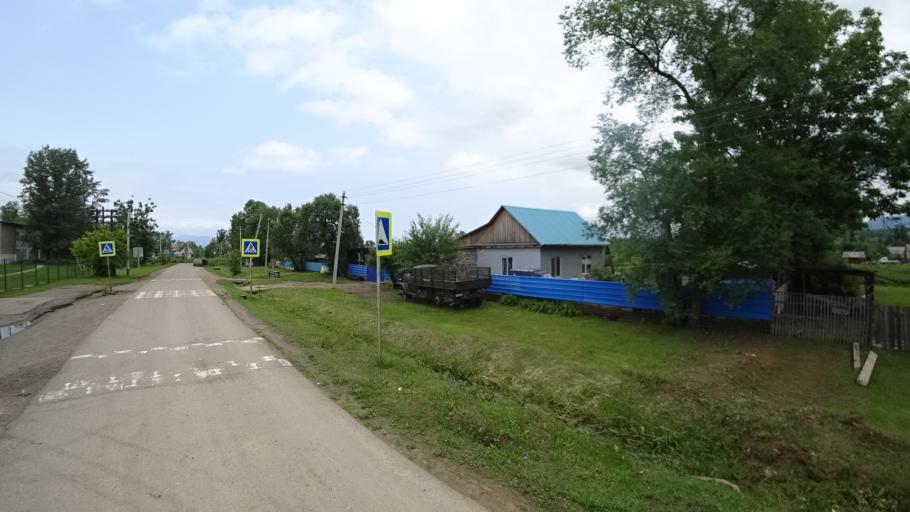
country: RU
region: Primorskiy
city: Novosysoyevka
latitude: 44.2385
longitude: 133.3643
